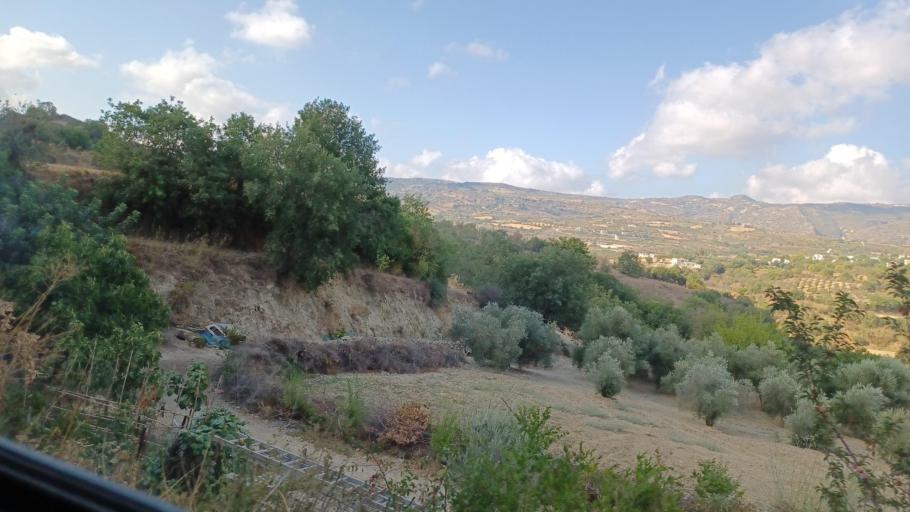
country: CY
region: Pafos
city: Tala
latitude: 34.9252
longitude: 32.4858
